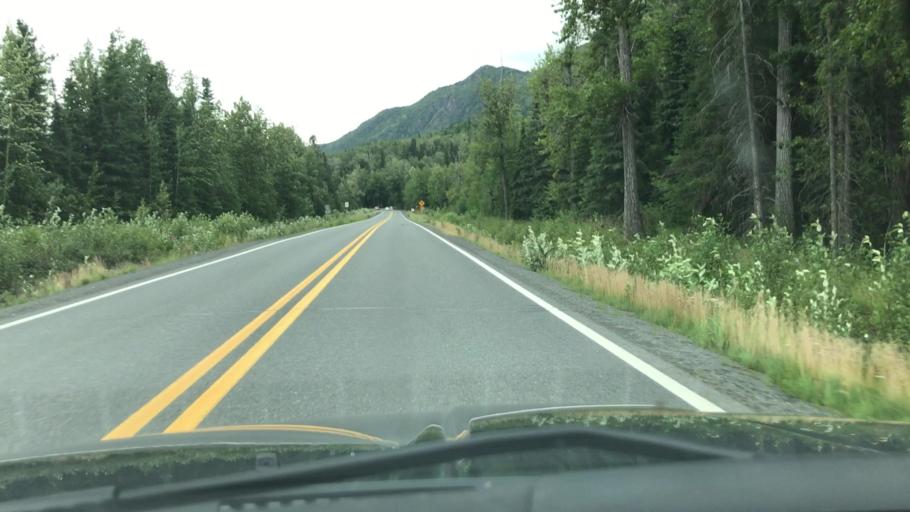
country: US
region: Alaska
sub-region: Kenai Peninsula Borough
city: Seward
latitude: 60.4873
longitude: -149.9715
